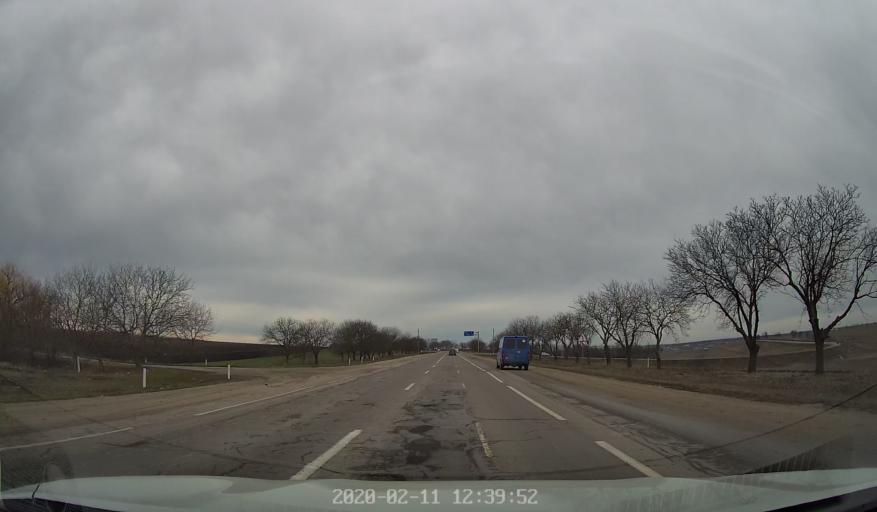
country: MD
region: Raionul Edinet
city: Edinet
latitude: 48.2049
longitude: 27.2651
